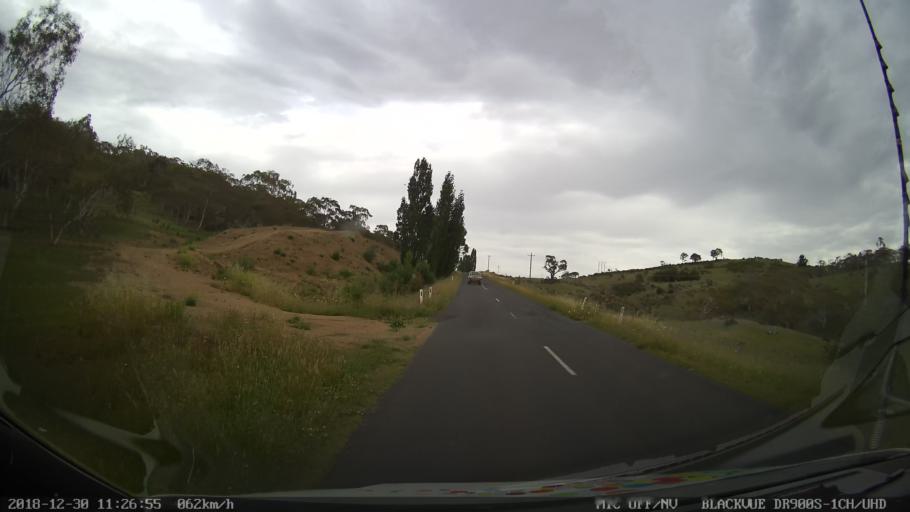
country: AU
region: New South Wales
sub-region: Snowy River
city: Jindabyne
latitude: -36.4645
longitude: 148.6302
